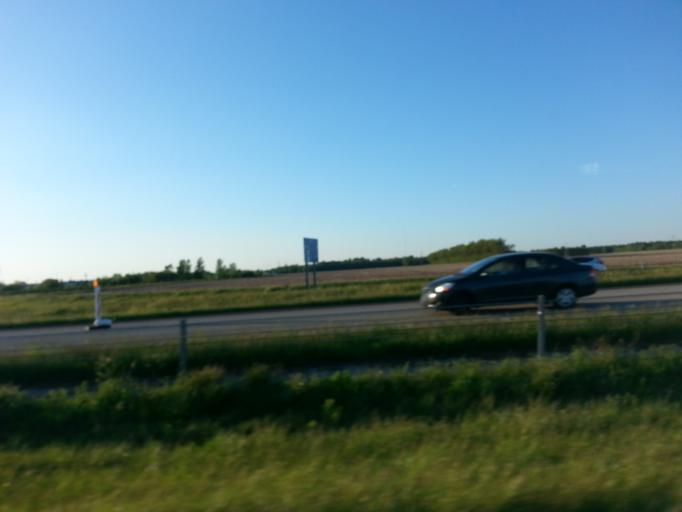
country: US
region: Illinois
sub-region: Vermilion County
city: Oakwood
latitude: 40.1268
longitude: -87.7753
